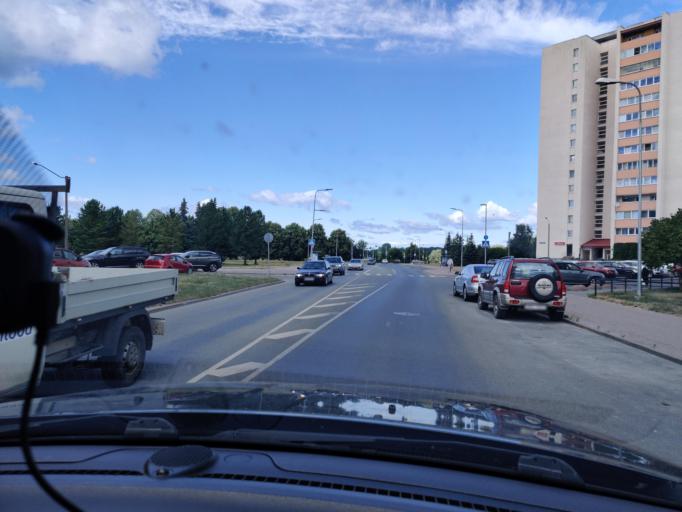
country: EE
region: Harju
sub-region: Saue vald
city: Laagri
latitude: 59.4082
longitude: 24.6331
